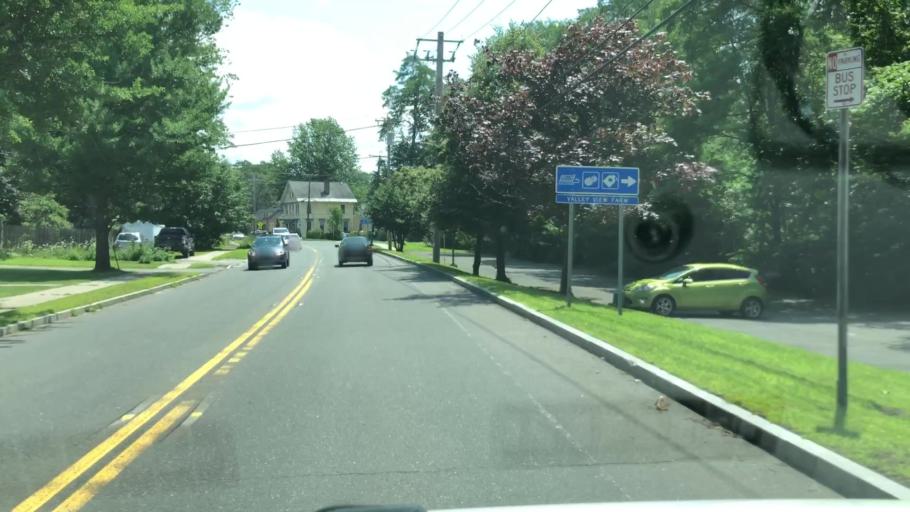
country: US
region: Massachusetts
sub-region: Hampshire County
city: Williamsburg
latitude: 42.3756
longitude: -72.7046
